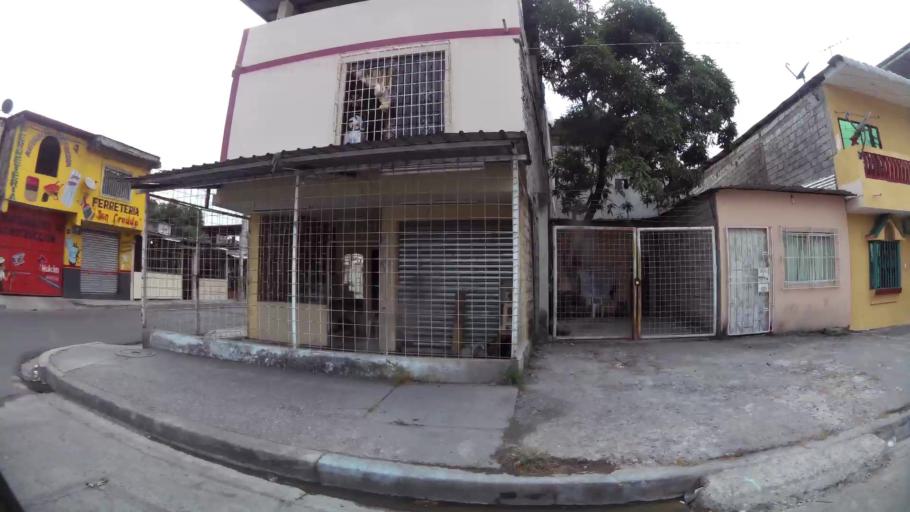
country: EC
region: Guayas
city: Guayaquil
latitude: -2.2364
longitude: -79.9065
